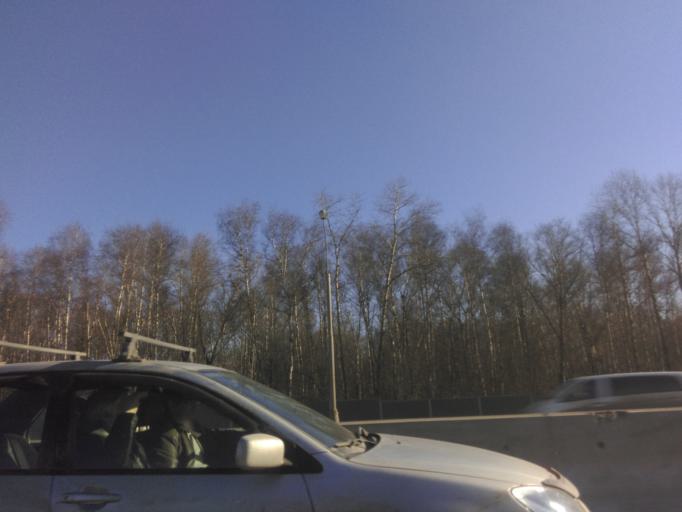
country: RU
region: Moskovskaya
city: Vostryakovo
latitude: 55.6557
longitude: 37.4396
